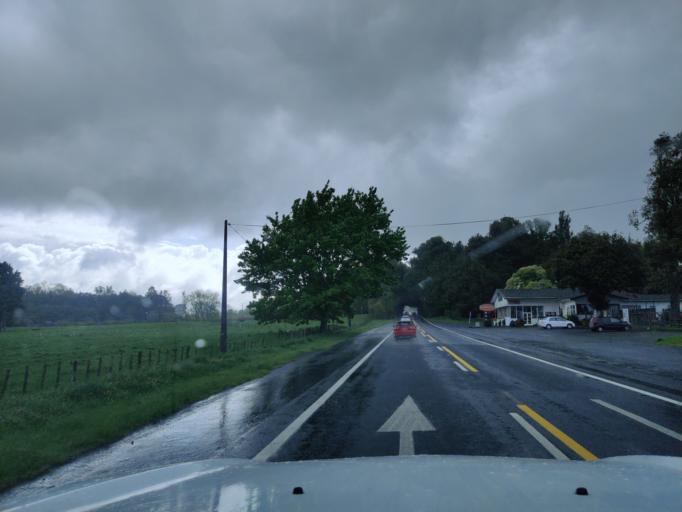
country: NZ
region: Waikato
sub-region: Matamata-Piako District
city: Matamata
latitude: -38.0007
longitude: 175.8888
